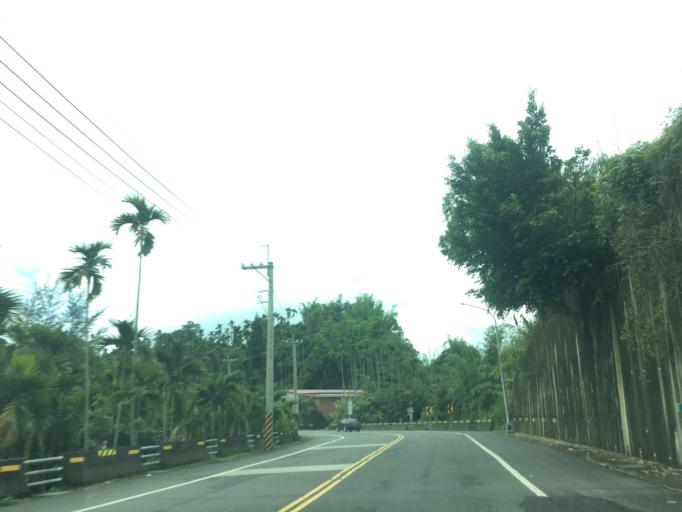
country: TW
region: Taiwan
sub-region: Yunlin
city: Douliu
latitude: 23.5749
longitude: 120.5644
